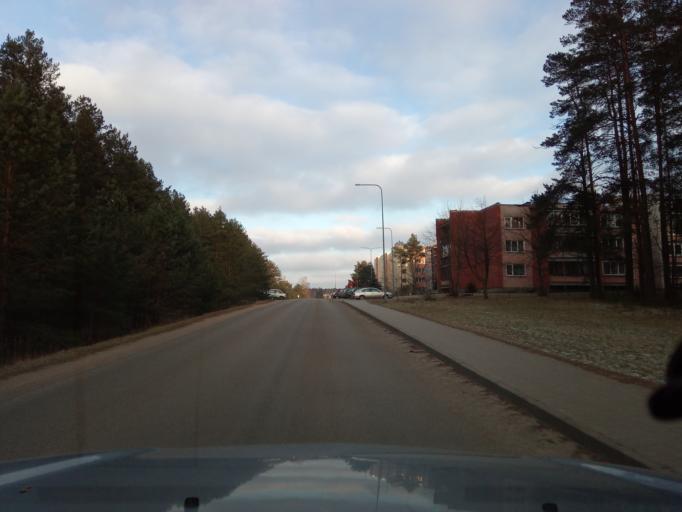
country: LT
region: Alytaus apskritis
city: Varena
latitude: 54.2141
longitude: 24.5557
